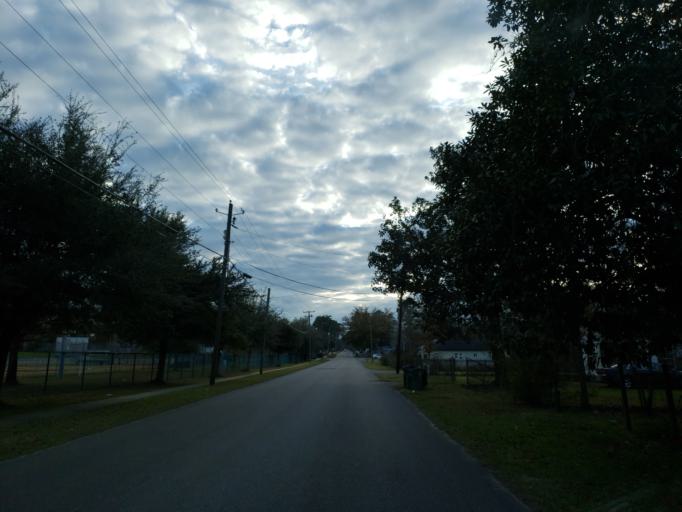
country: US
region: Mississippi
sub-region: Forrest County
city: Hattiesburg
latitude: 31.3084
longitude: -89.3066
